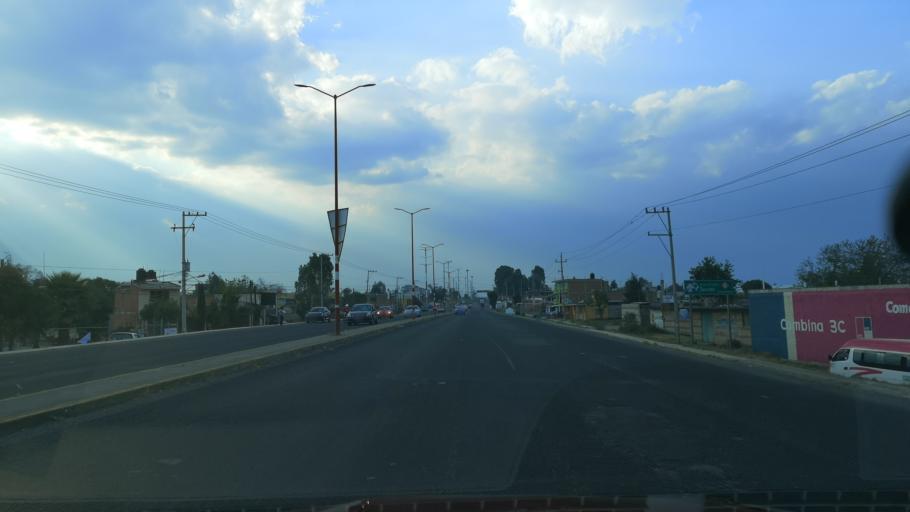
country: MX
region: Puebla
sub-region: Juan C. Bonilla
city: Santa Maria Zacatepec
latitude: 19.1257
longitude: -98.3677
